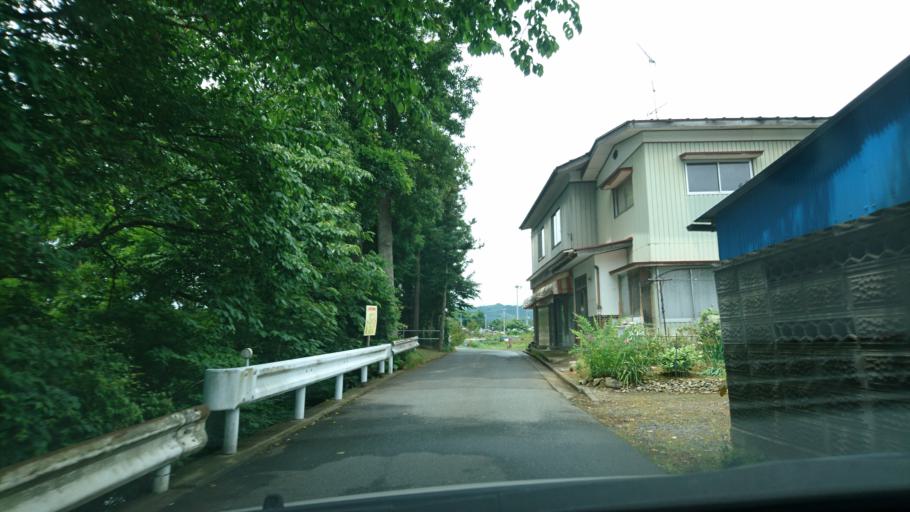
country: JP
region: Iwate
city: Ichinoseki
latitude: 38.9299
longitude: 141.1108
